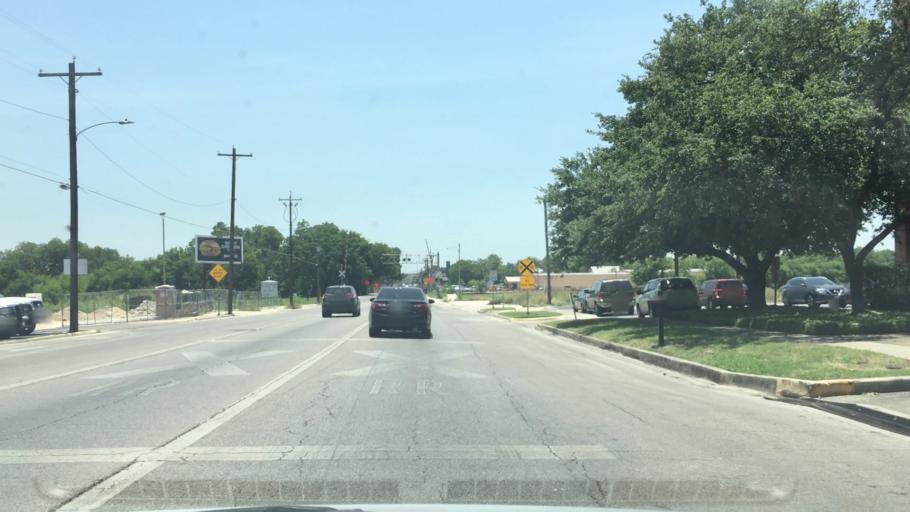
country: US
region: Texas
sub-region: Hays County
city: San Marcos
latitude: 29.8799
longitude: -97.9410
